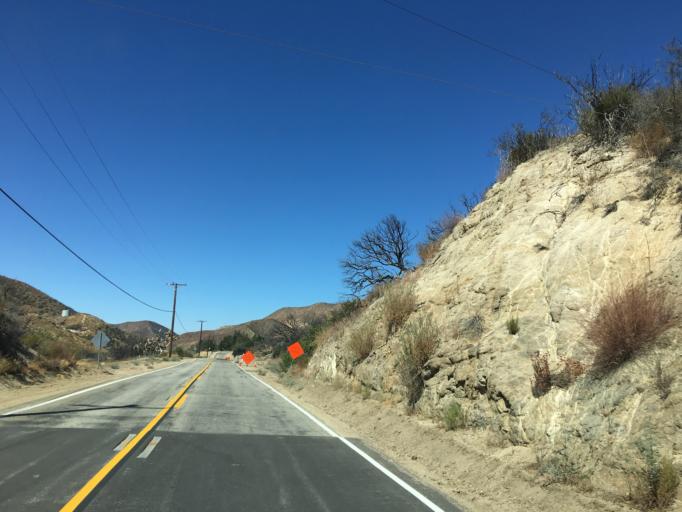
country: US
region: California
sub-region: Los Angeles County
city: Green Valley
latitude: 34.6549
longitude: -118.4681
